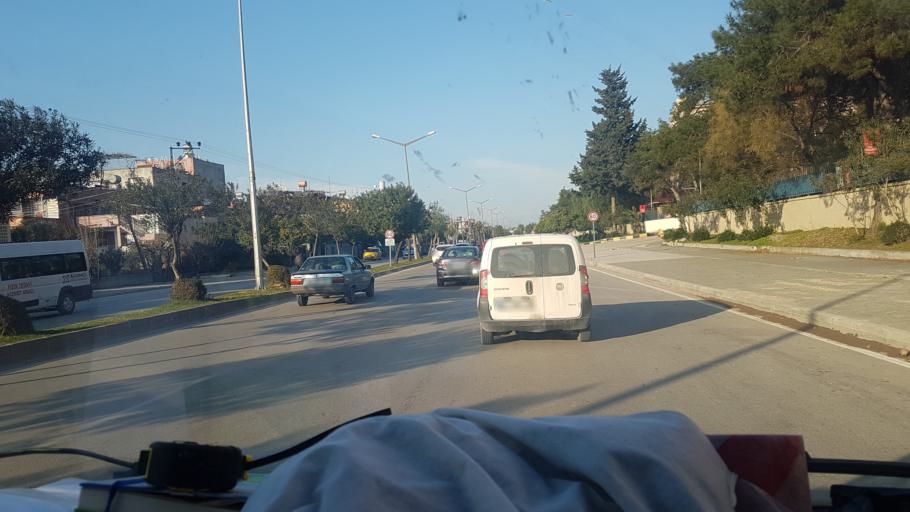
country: TR
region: Adana
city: Adana
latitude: 37.0152
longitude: 35.3395
